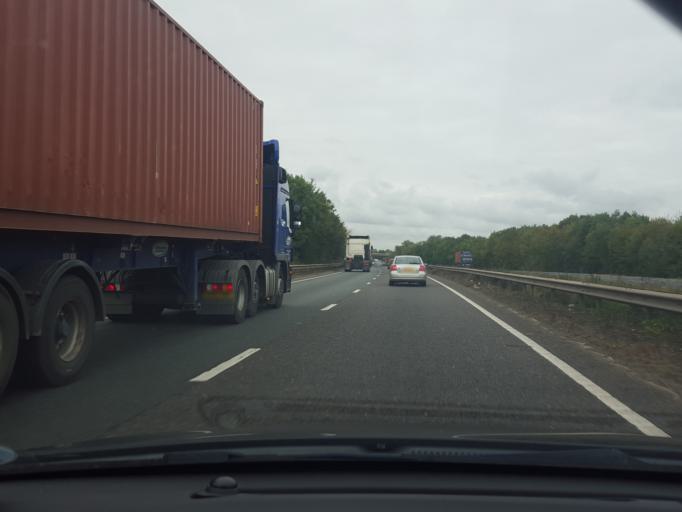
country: GB
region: England
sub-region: Suffolk
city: Bramford
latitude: 52.1128
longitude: 1.1051
